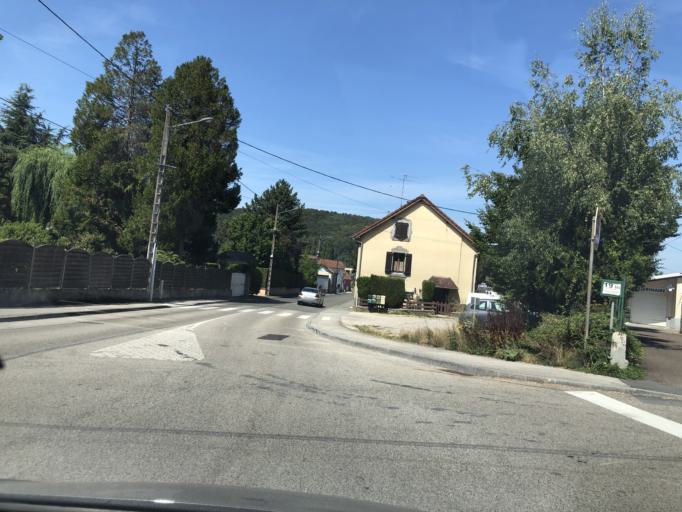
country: FR
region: Franche-Comte
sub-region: Departement du Doubs
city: Voujeaucourt
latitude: 47.4721
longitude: 6.7654
